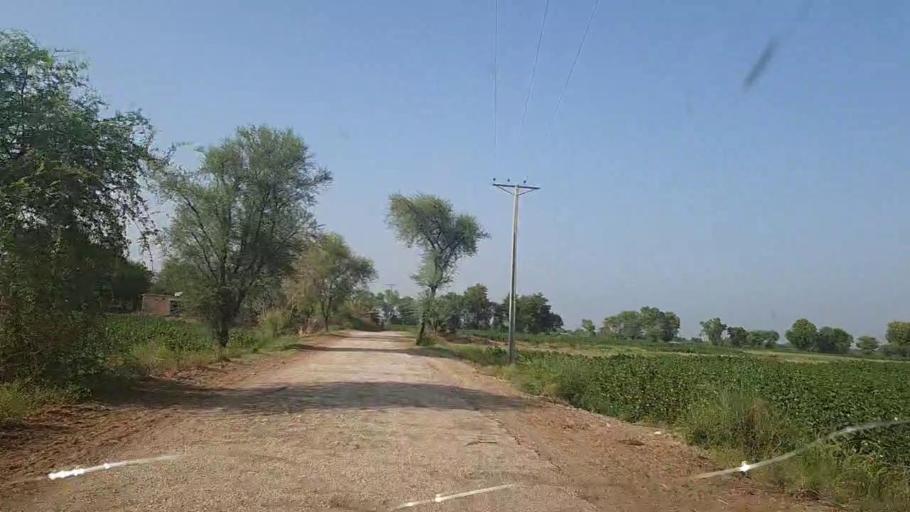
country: PK
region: Sindh
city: Khanpur
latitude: 27.7282
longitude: 69.3317
